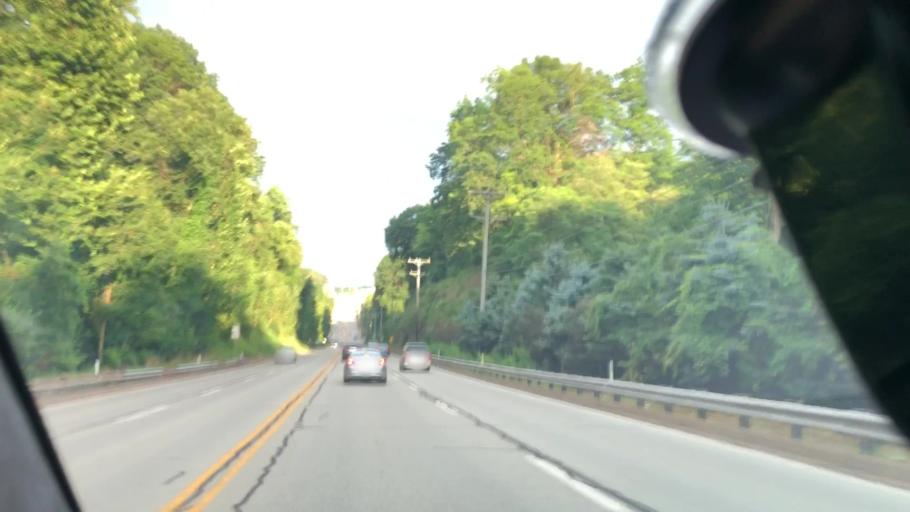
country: US
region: Pennsylvania
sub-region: Allegheny County
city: Churchill
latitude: 40.4365
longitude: -79.8268
